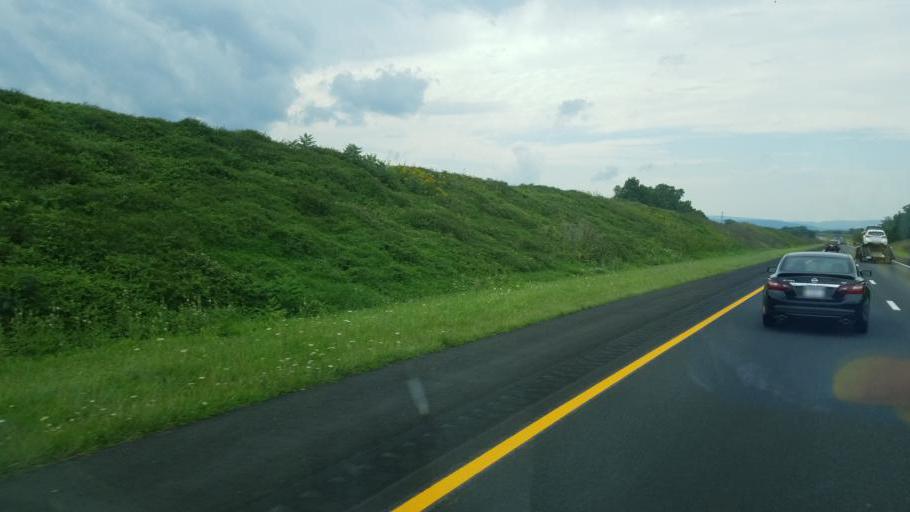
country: US
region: Virginia
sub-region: Frederick County
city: Middletown
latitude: 38.9857
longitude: -78.2358
